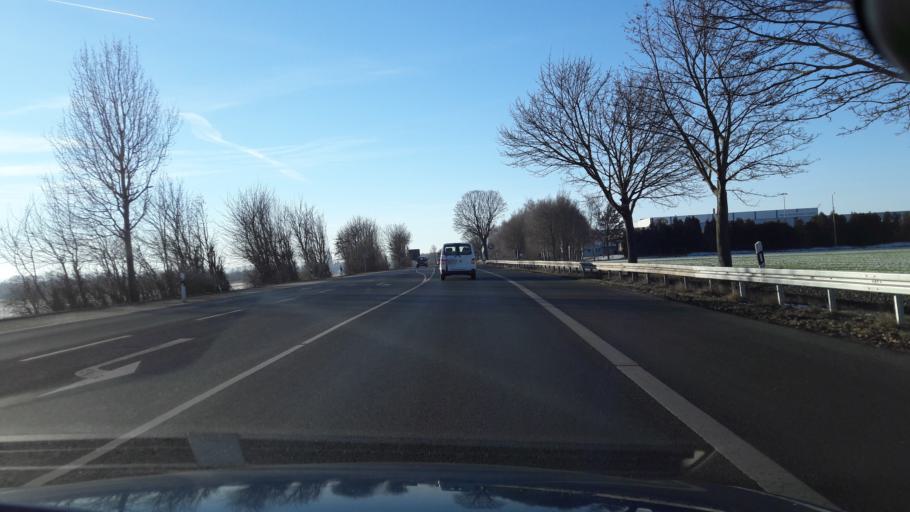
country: DE
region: North Rhine-Westphalia
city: Erwitte
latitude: 51.6319
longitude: 8.3413
